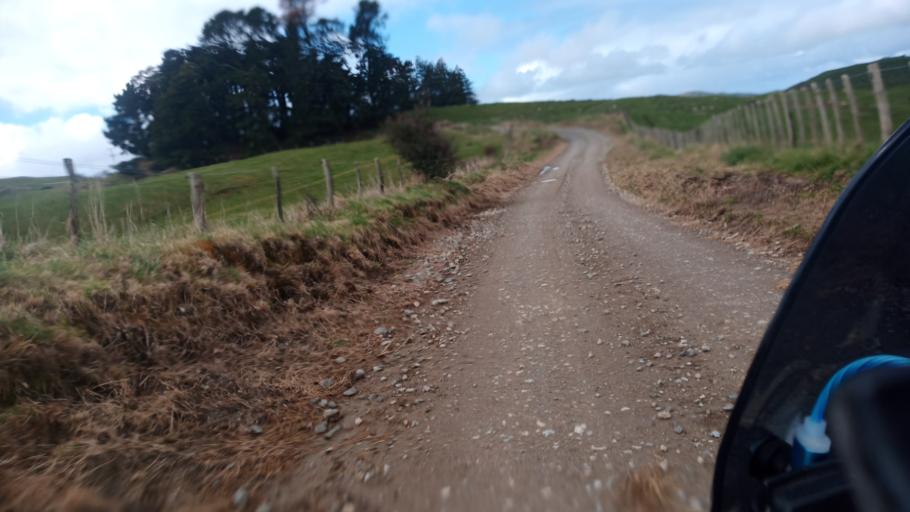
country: NZ
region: Gisborne
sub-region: Gisborne District
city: Gisborne
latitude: -38.5007
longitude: 178.2033
